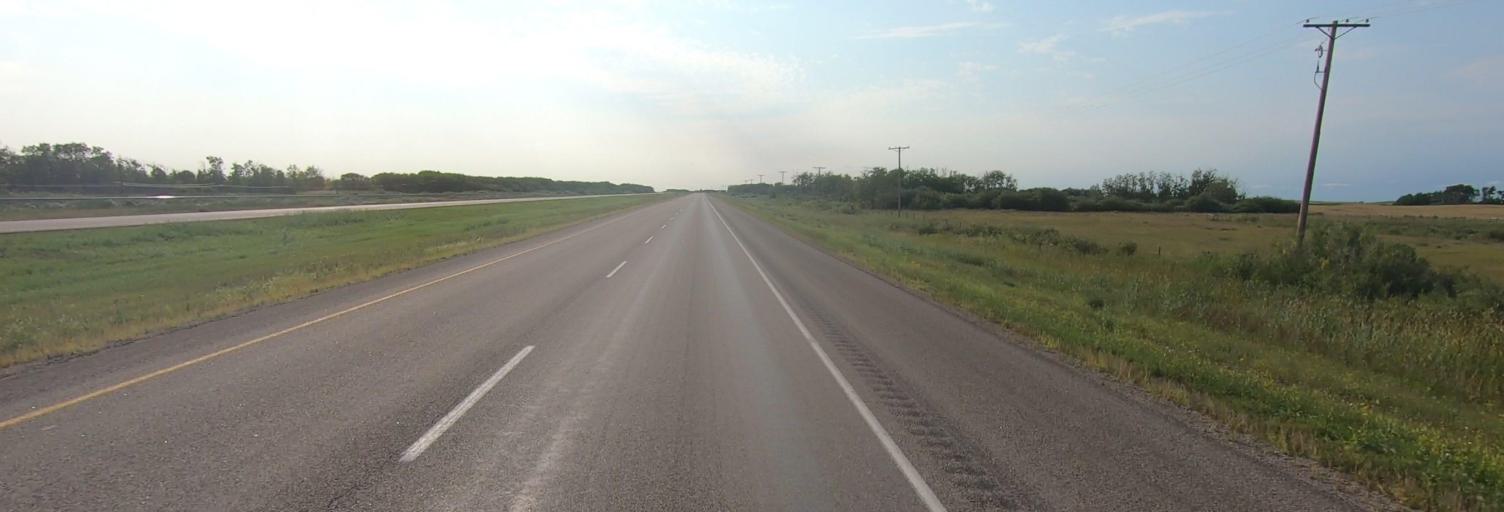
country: CA
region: Saskatchewan
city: Esterhazy
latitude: 50.3703
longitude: -102.4591
